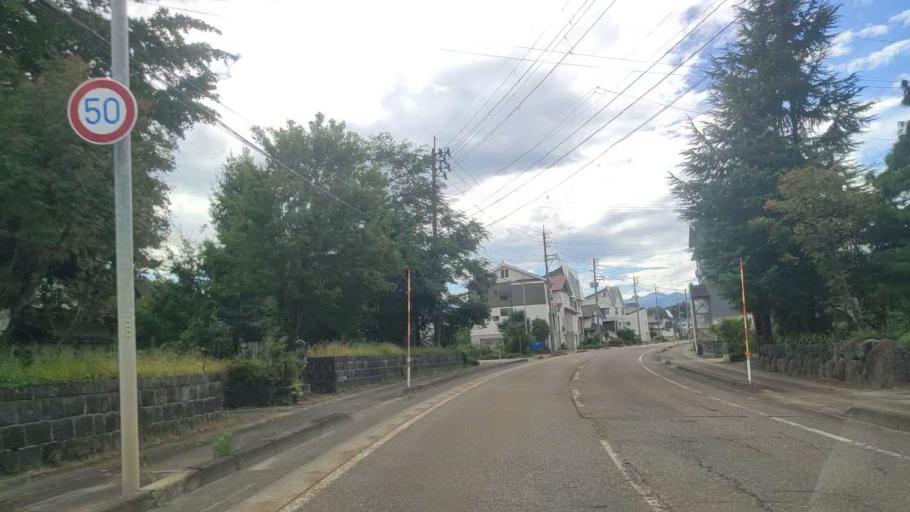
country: JP
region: Niigata
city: Arai
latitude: 36.9853
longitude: 138.2723
